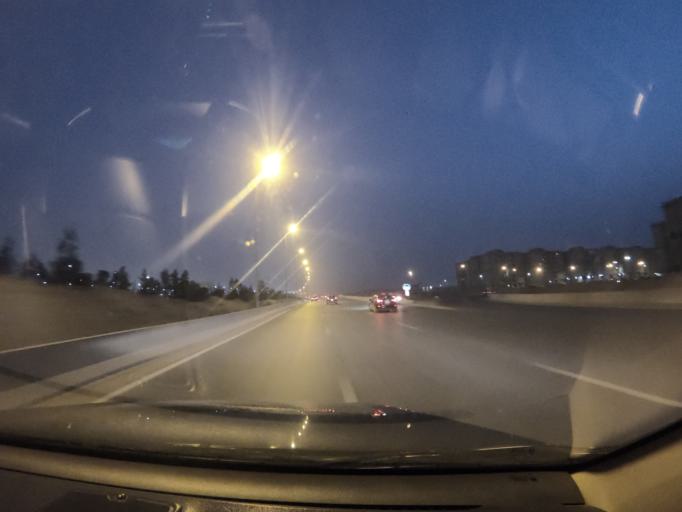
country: EG
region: Muhafazat al Qahirah
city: Cairo
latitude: 30.0384
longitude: 31.4029
